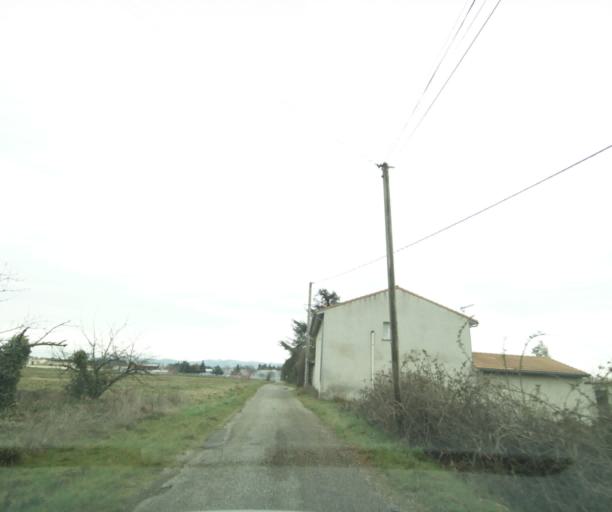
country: FR
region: Rhone-Alpes
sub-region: Departement de la Drome
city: Bourg-les-Valence
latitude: 44.9723
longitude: 4.8917
